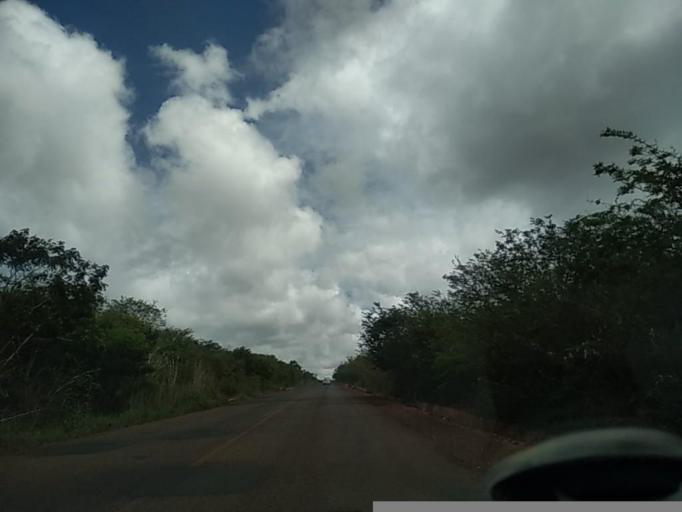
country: BR
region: Bahia
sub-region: Caetite
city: Caetite
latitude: -14.0389
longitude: -42.4864
